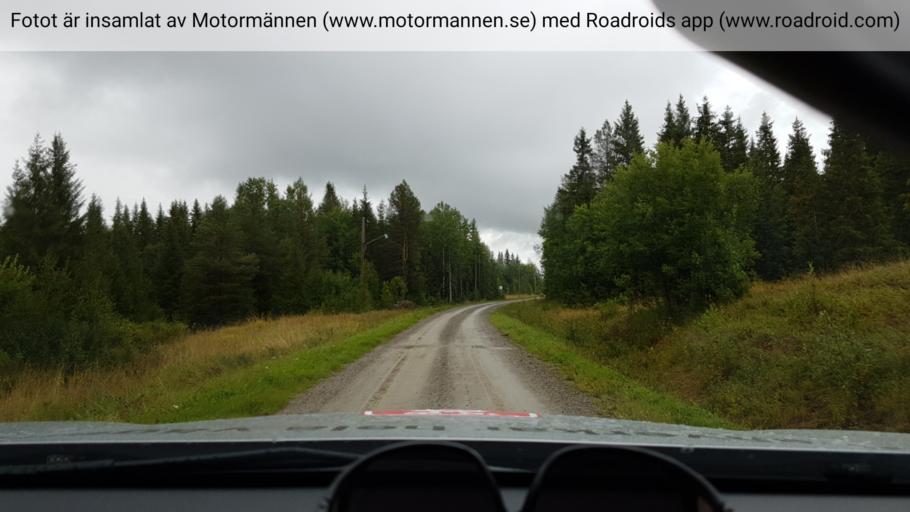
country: SE
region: Vaesterbotten
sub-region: Asele Kommun
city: Insjon
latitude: 64.8003
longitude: 17.4819
